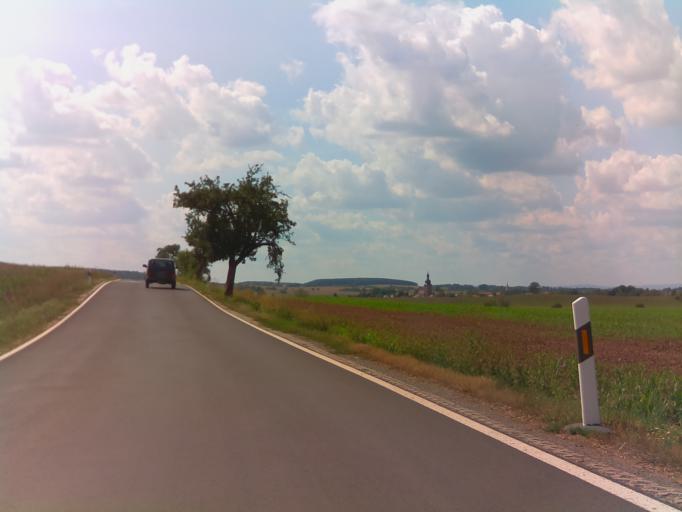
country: DE
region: Thuringia
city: Gleichamberg
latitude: 50.3466
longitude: 10.5902
